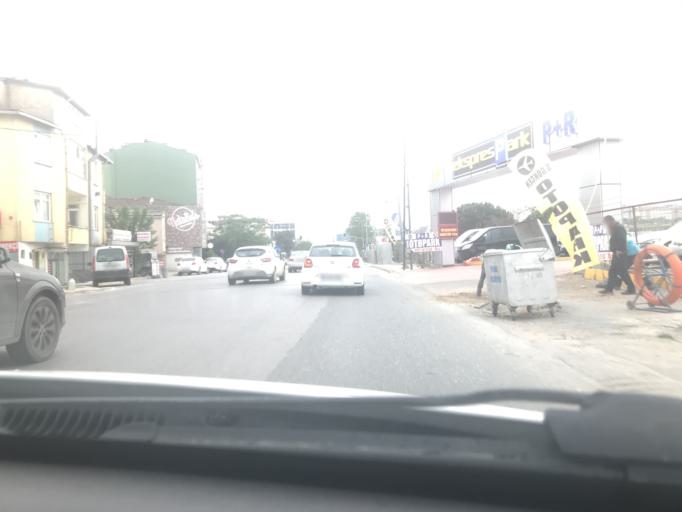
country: TR
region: Istanbul
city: Sultanbeyli
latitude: 40.9297
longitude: 29.3254
